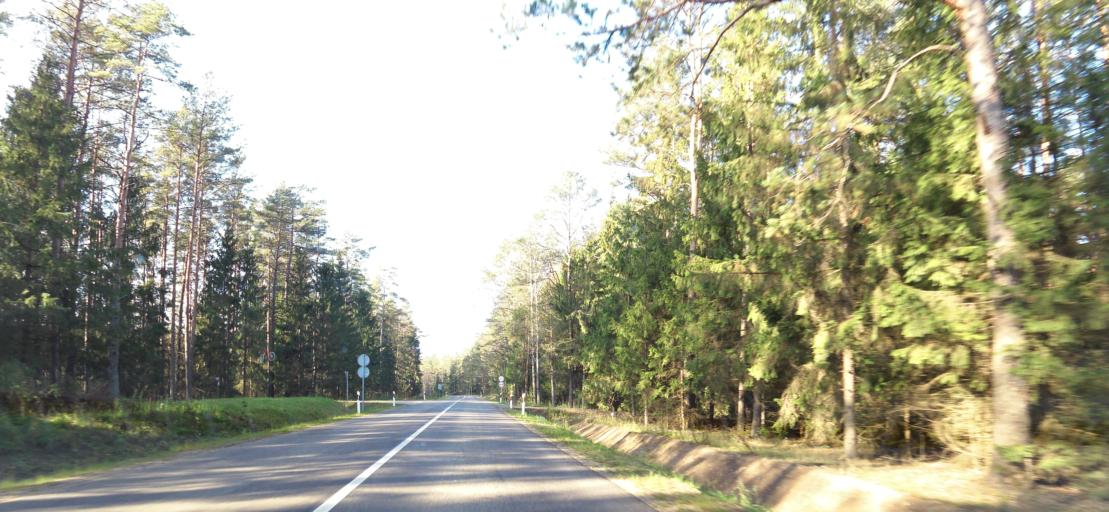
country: LT
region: Vilnius County
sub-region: Trakai
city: Rudiskes
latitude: 54.5096
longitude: 24.8898
